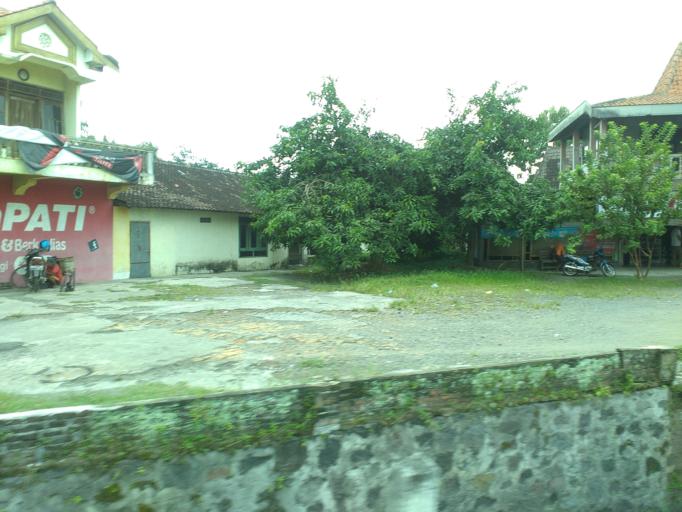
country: ID
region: Central Java
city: Ceper
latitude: -7.6643
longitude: 110.6668
